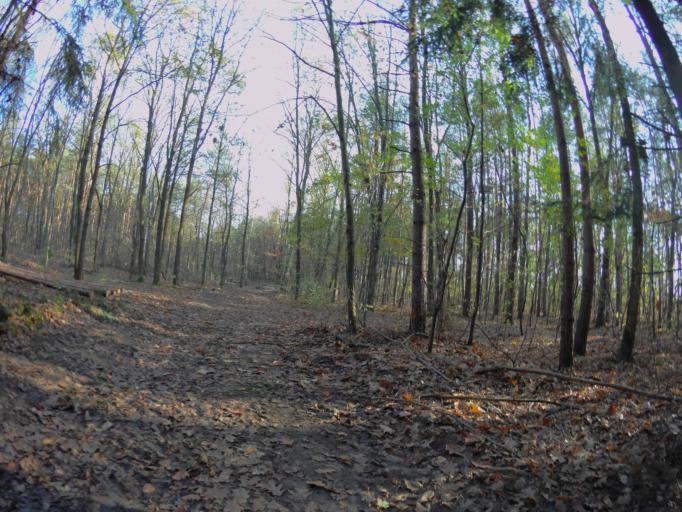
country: PL
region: Subcarpathian Voivodeship
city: Nowa Sarzyna
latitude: 50.3054
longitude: 22.3550
